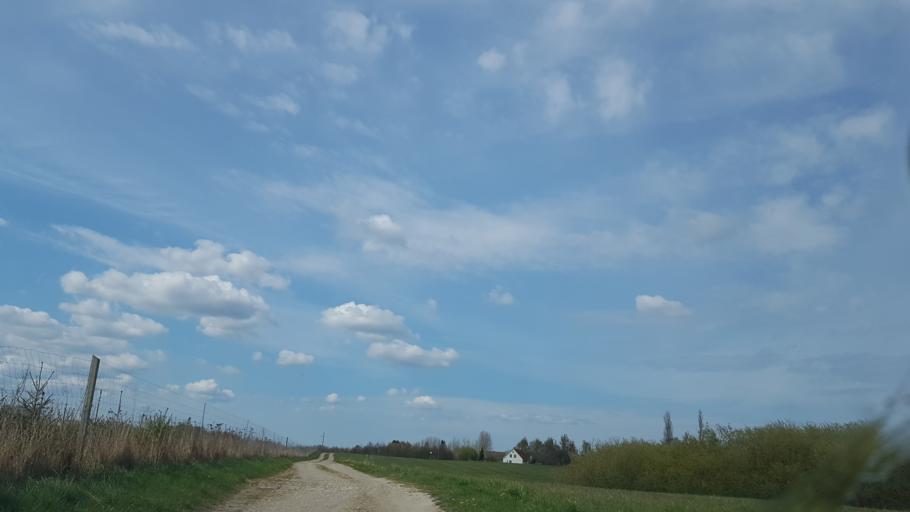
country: DK
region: Capital Region
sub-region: Allerod Kommune
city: Lillerod
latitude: 55.8970
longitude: 12.3361
